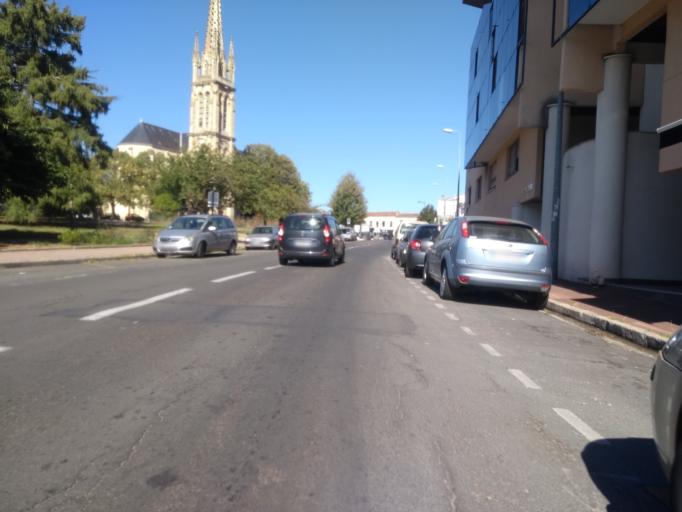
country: FR
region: Aquitaine
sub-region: Departement de la Gironde
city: Le Bouscat
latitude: 44.8507
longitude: -0.6140
